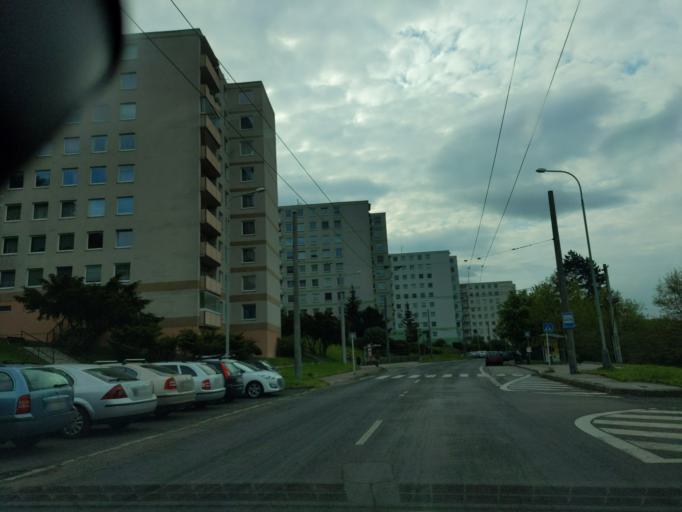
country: CZ
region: Ustecky
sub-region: Okres Usti nad Labem
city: Usti nad Labem
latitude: 50.6791
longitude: 14.0150
